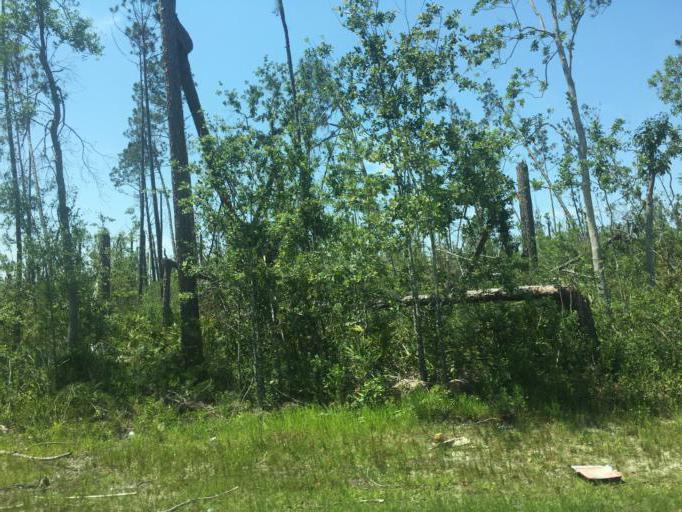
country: US
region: Florida
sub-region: Bay County
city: Hiland Park
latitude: 30.2185
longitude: -85.6319
